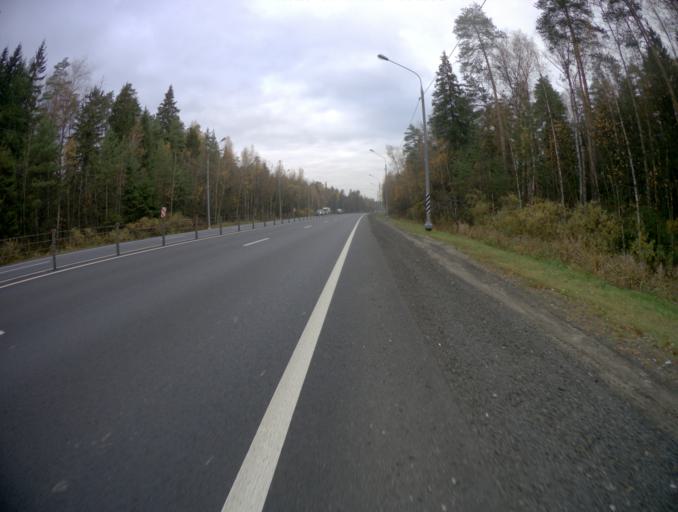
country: RU
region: Moskovskaya
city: Malaya Dubna
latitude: 55.8551
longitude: 38.9627
